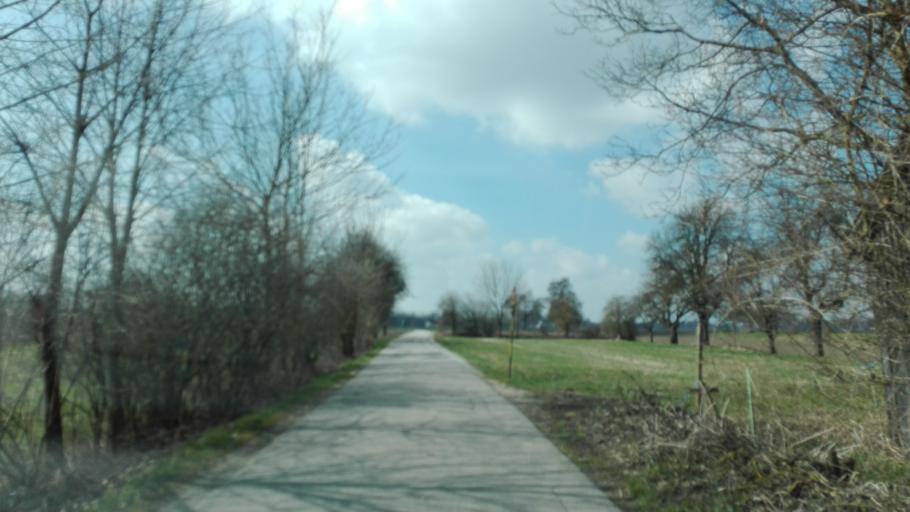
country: AT
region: Upper Austria
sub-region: Politischer Bezirk Urfahr-Umgebung
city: Ottensheim
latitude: 48.3282
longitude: 14.1524
